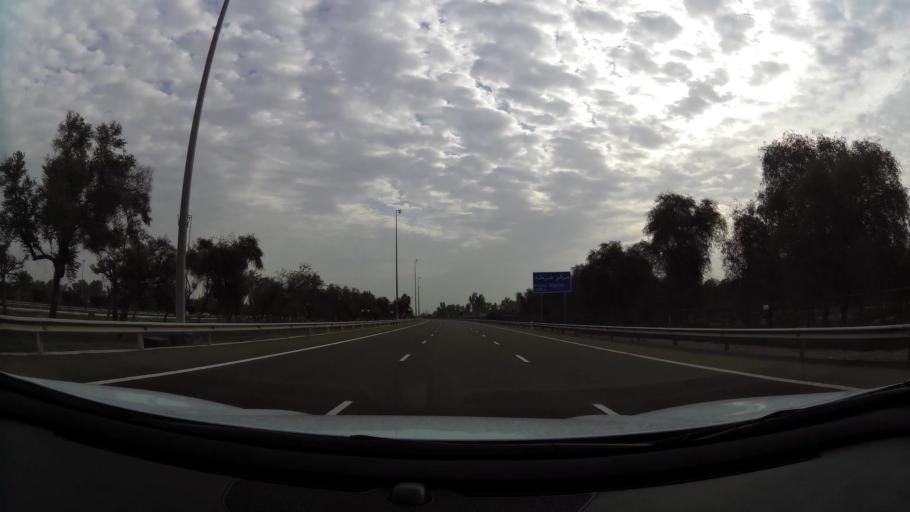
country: AE
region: Abu Dhabi
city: Al Ain
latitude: 24.1747
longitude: 55.2997
